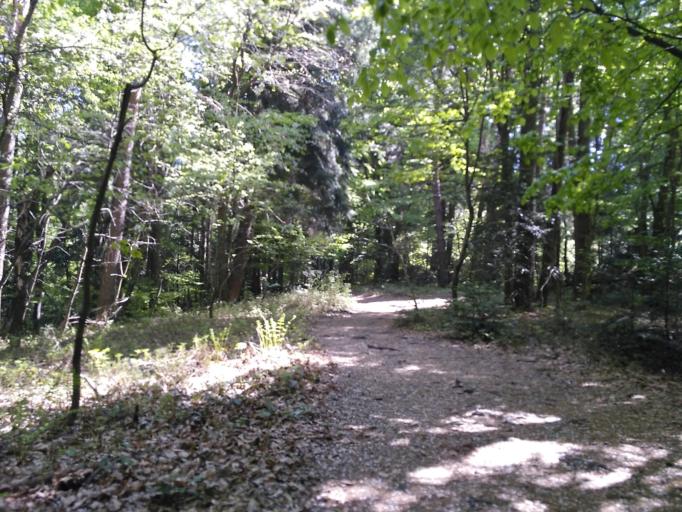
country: PL
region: Subcarpathian Voivodeship
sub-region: Powiat krosnienski
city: Korczyna
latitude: 49.7428
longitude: 21.8093
